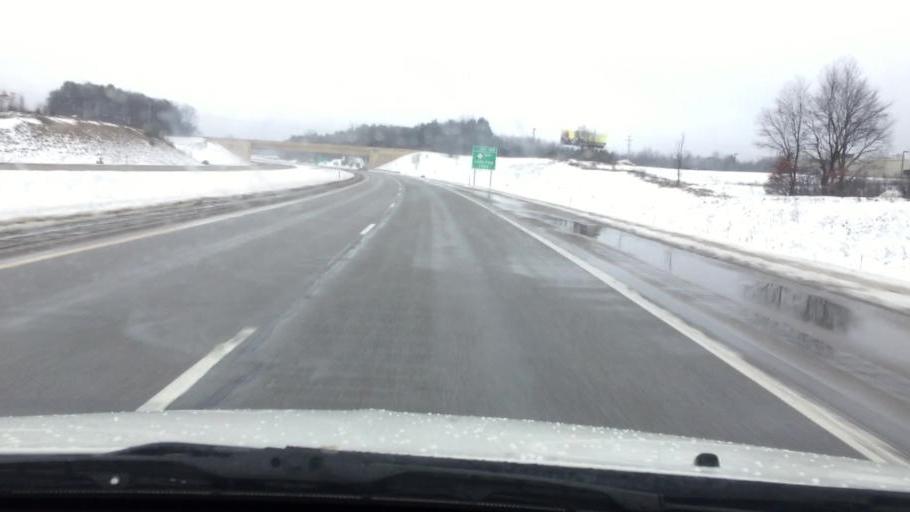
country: US
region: Michigan
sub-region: Wexford County
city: Cadillac
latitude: 44.2699
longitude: -85.3886
